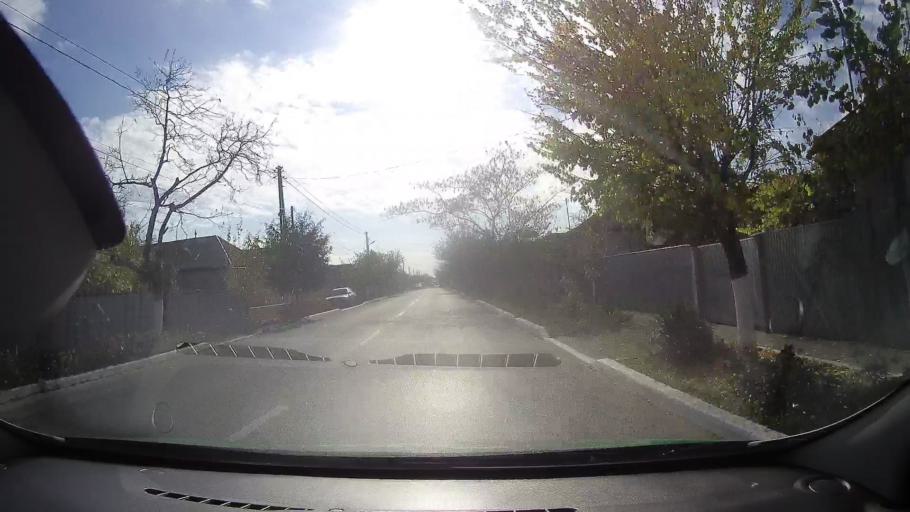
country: RO
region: Tulcea
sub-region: Comuna Sarichioi
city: Sarichioi
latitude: 44.9496
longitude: 28.8517
